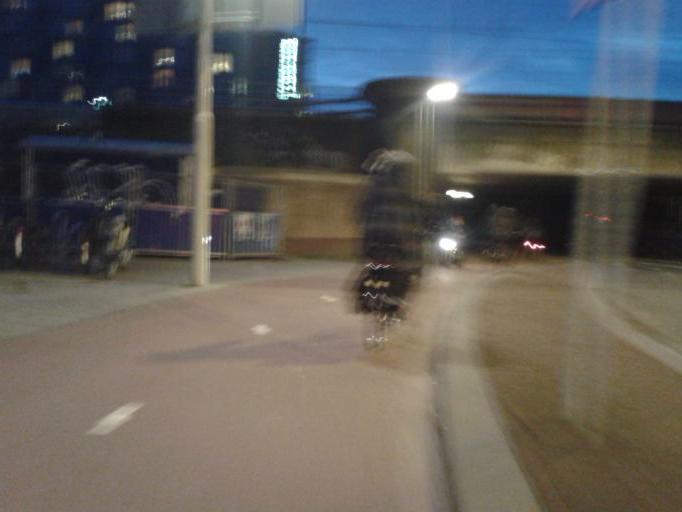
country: NL
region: North Holland
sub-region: Gemeente Amsterdam
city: Amsterdam
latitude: 52.3780
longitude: 4.9050
